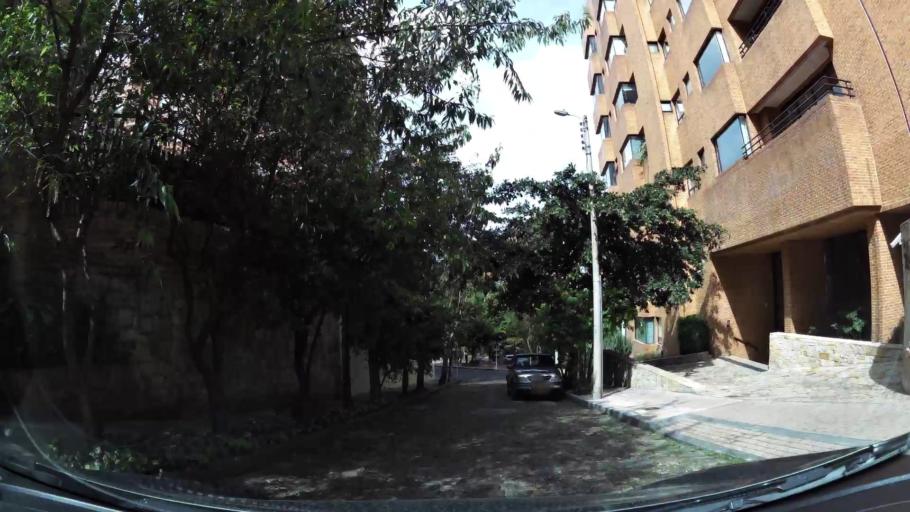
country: CO
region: Bogota D.C.
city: Barrio San Luis
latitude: 4.6567
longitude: -74.0505
